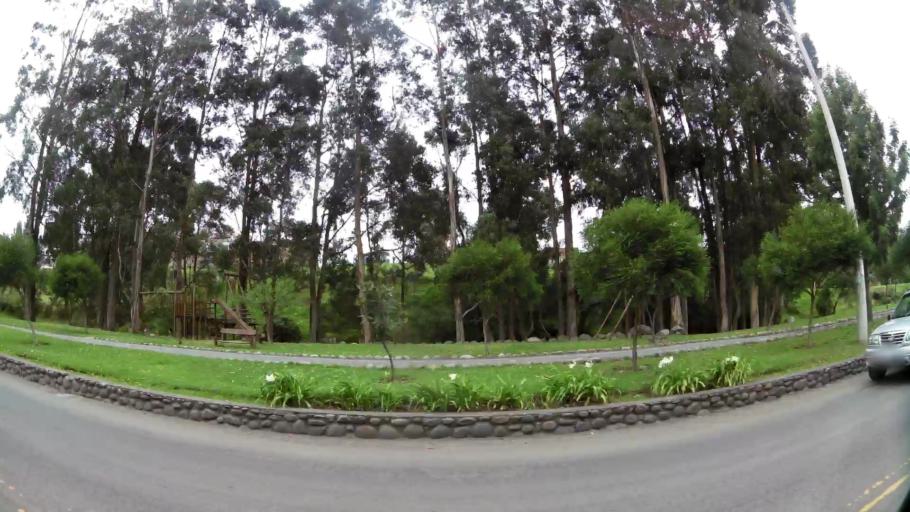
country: EC
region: Azuay
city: Cuenca
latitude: -2.9087
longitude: -79.0206
